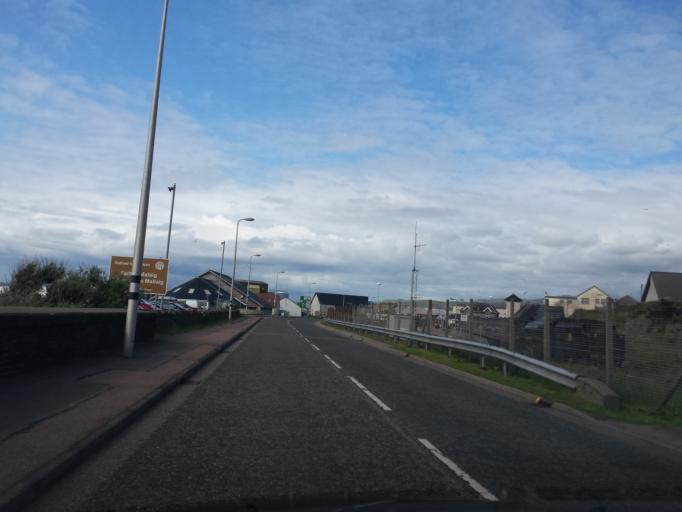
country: GB
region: Scotland
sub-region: Highland
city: Portree
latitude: 57.0045
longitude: -5.8316
